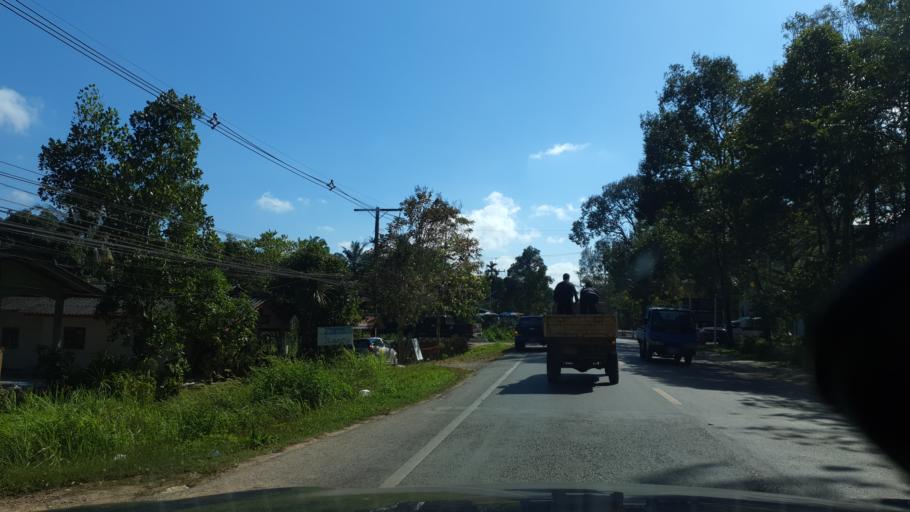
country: TH
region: Phangnga
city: Ban Ao Nang
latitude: 8.0297
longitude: 98.8664
